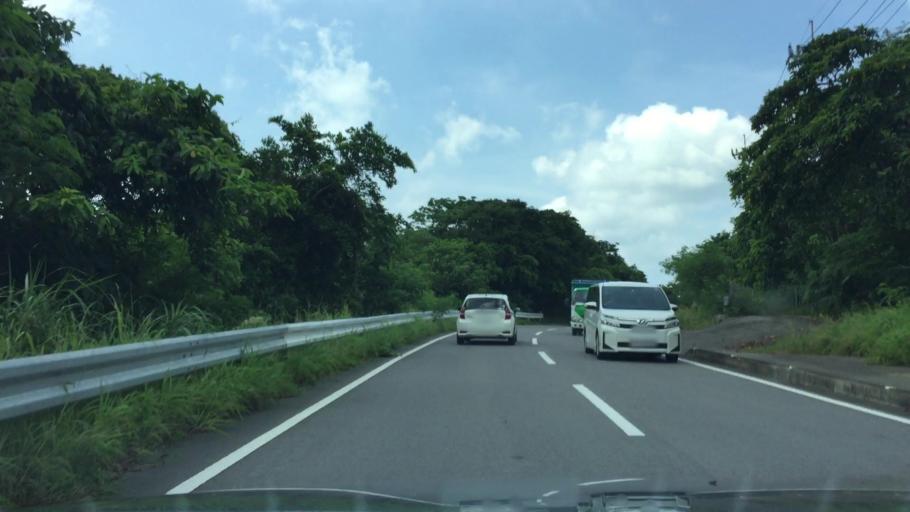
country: JP
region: Okinawa
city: Ishigaki
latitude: 24.4584
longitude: 124.2266
